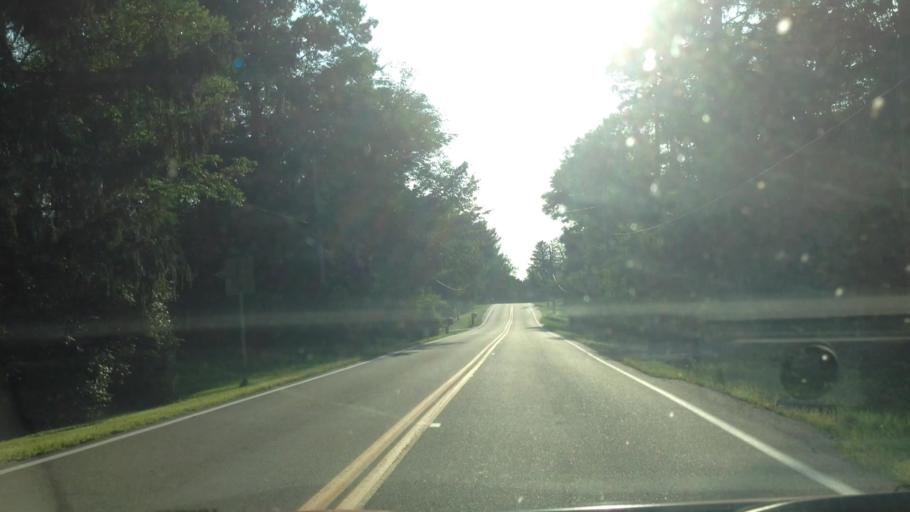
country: US
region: Ohio
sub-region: Summit County
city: Fairlawn
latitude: 41.1453
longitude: -81.6079
